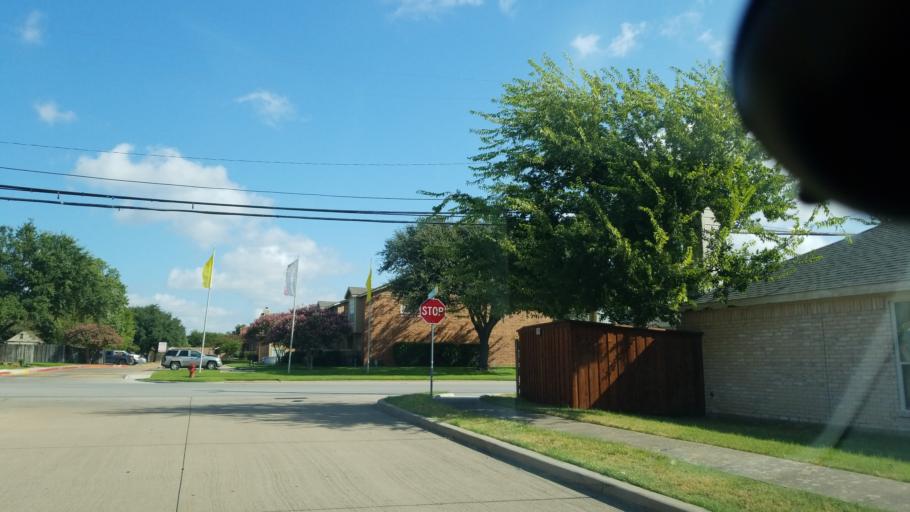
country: US
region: Texas
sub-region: Dallas County
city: Grand Prairie
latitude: 32.6986
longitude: -96.9964
